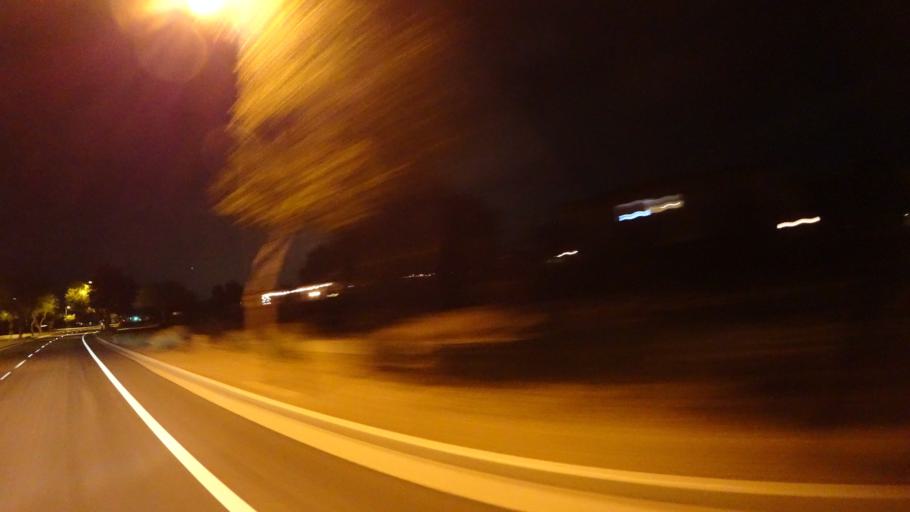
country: US
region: Arizona
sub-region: Maricopa County
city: Queen Creek
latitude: 33.2656
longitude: -111.6788
